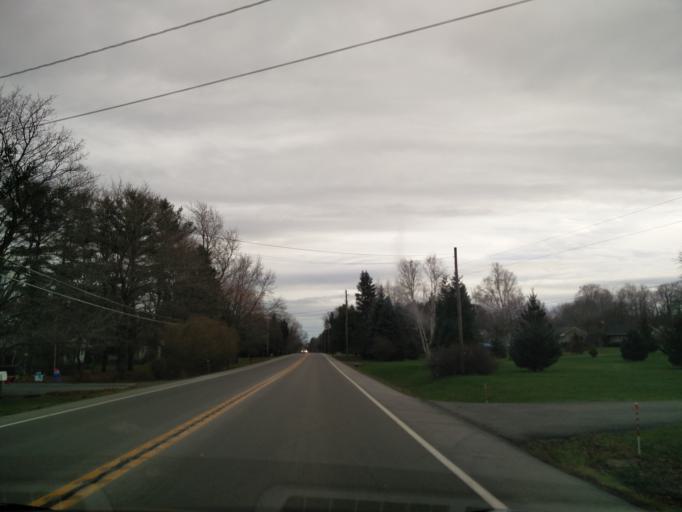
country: US
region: New York
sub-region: Tompkins County
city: Northwest Ithaca
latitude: 42.4792
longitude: -76.5599
